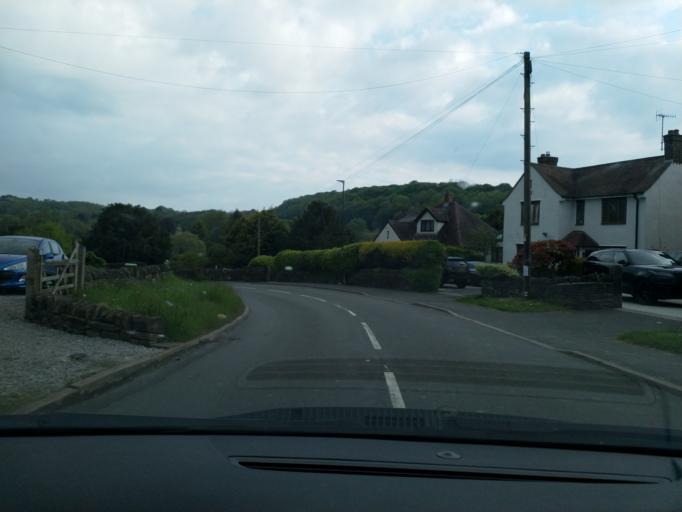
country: GB
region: England
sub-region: Derbyshire
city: Dronfield
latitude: 53.2757
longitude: -1.4963
